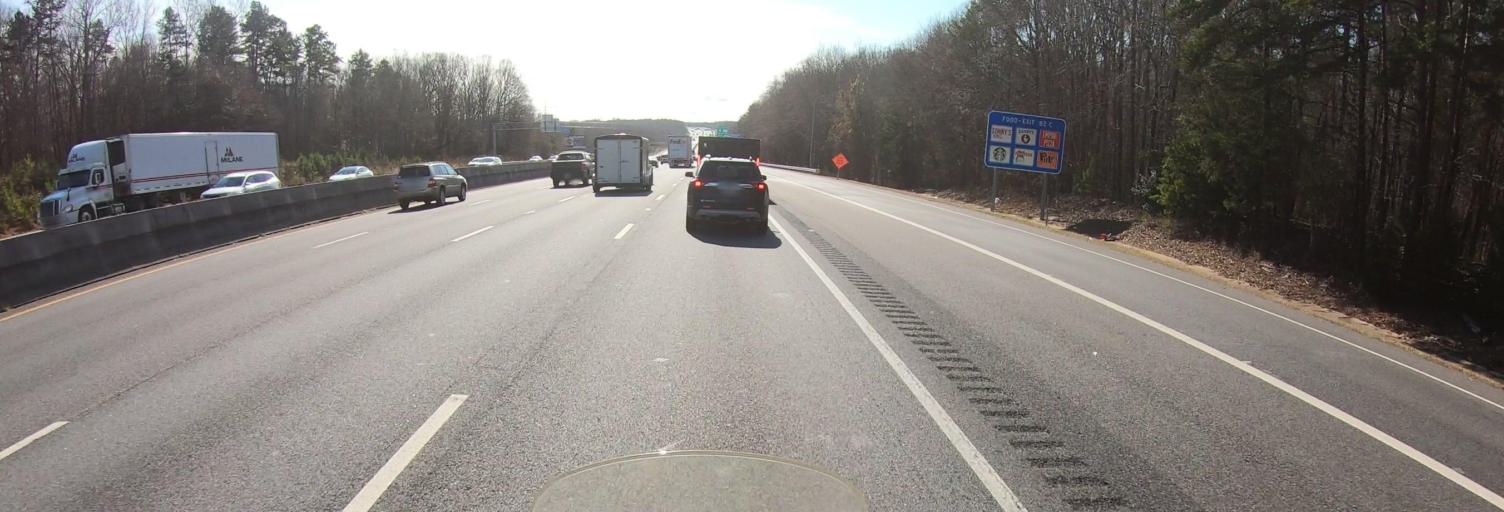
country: US
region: South Carolina
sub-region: York County
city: Fort Mill
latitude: 34.9963
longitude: -80.9779
